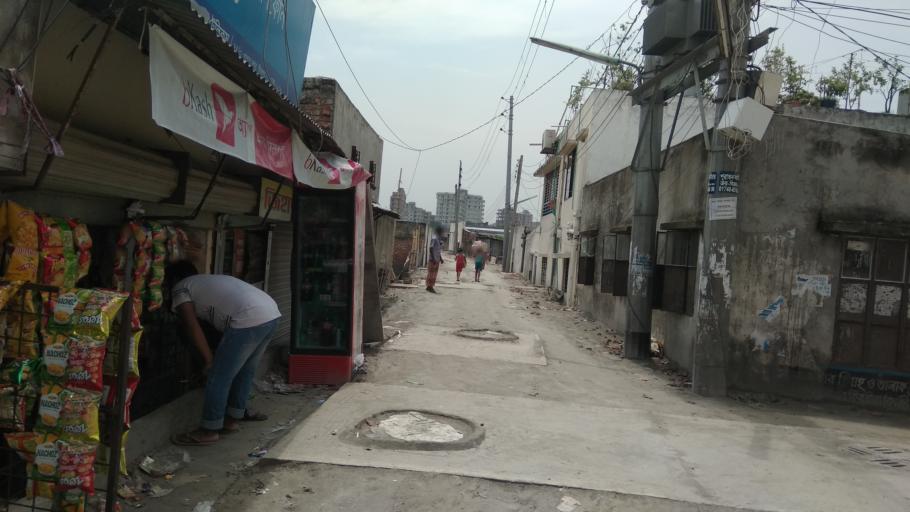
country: BD
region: Dhaka
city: Tungi
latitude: 23.8160
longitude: 90.3808
